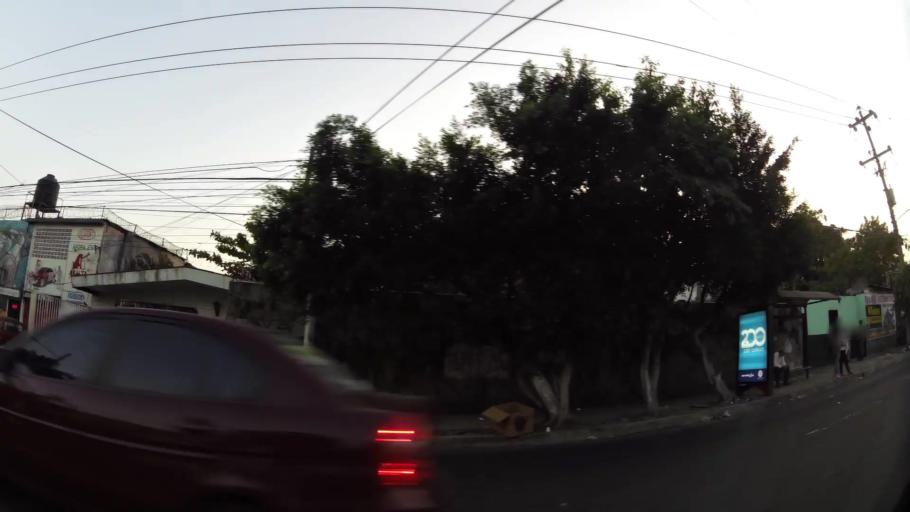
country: SV
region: San Salvador
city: Mejicanos
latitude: 13.7177
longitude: -89.2216
